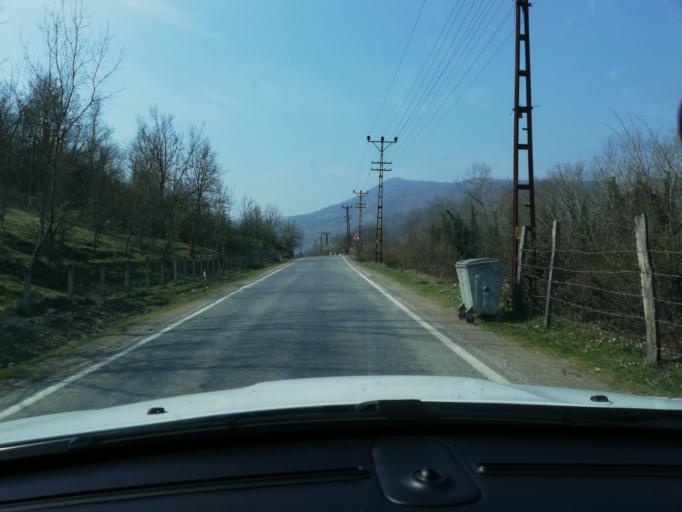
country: TR
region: Karabuk
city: Yenice
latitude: 41.2578
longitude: 32.3614
